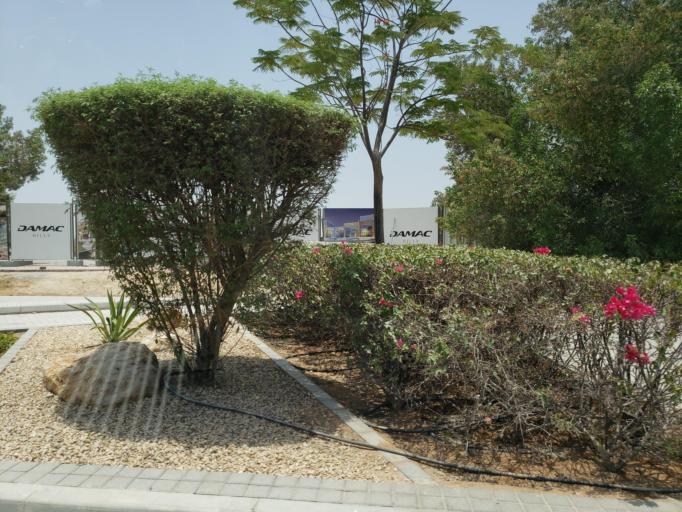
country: AE
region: Dubai
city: Dubai
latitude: 25.0283
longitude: 55.2520
